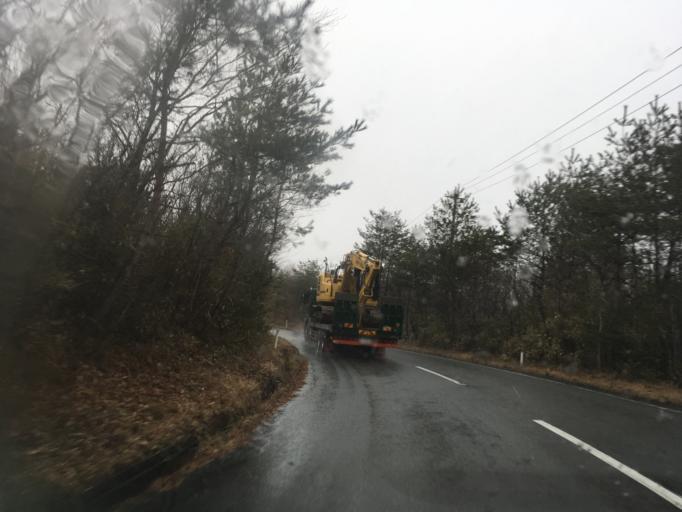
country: JP
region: Iwate
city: Ichinoseki
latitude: 38.8503
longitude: 141.0362
